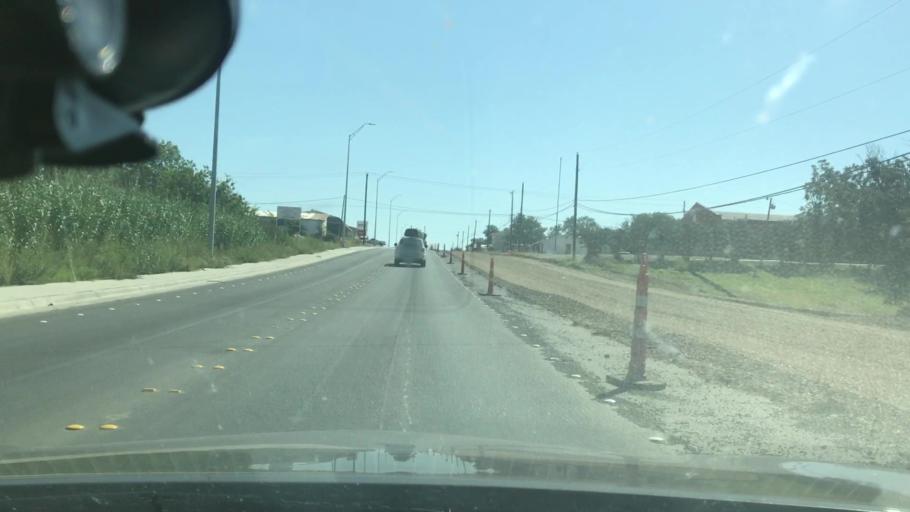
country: US
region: Texas
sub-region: Stephens County
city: Breckenridge
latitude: 32.7554
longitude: -98.8954
